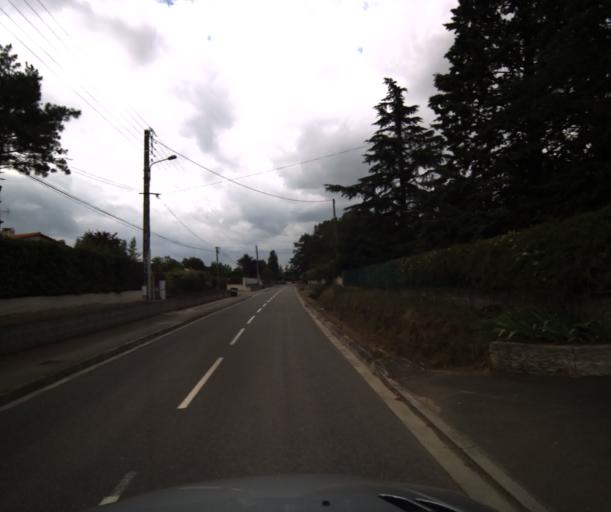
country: FR
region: Midi-Pyrenees
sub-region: Departement de la Haute-Garonne
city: Labarthe-sur-Leze
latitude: 43.4433
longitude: 1.3975
